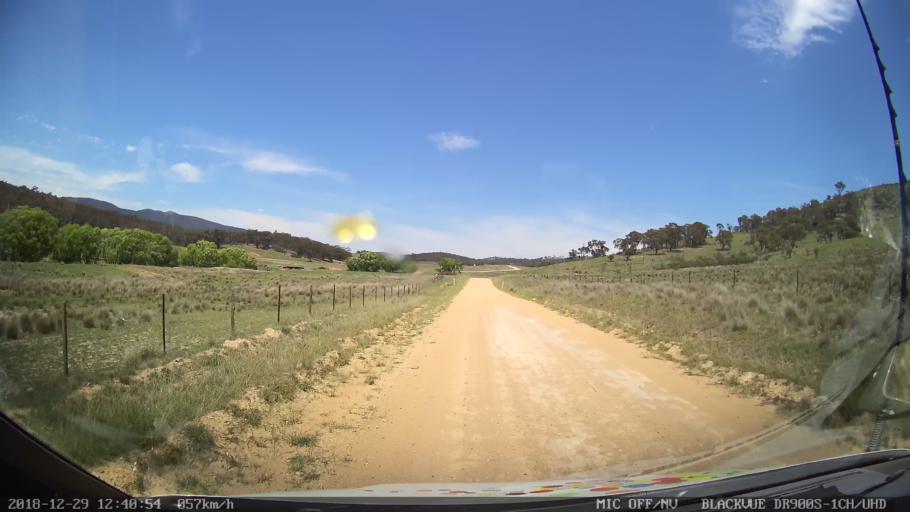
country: AU
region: Australian Capital Territory
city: Macarthur
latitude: -35.6048
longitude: 149.2234
